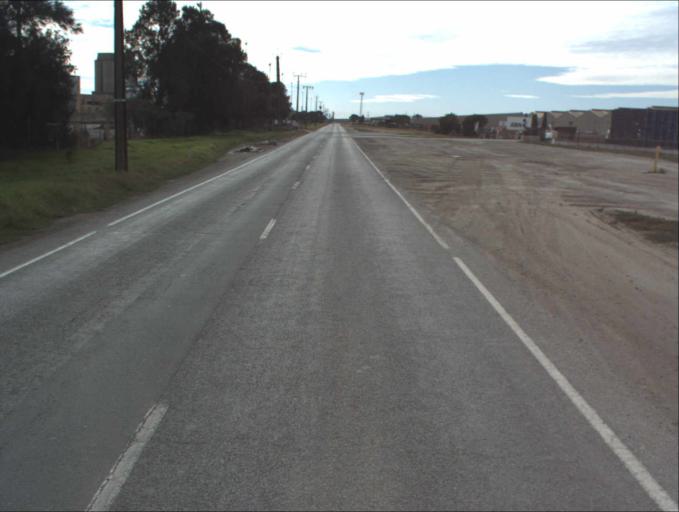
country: AU
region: South Australia
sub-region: Port Adelaide Enfield
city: Birkenhead
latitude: -34.8335
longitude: 138.5161
